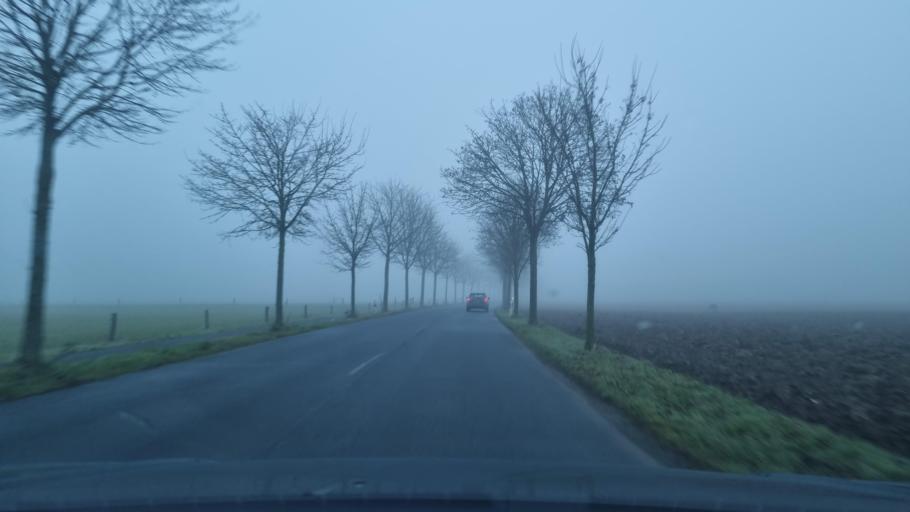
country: DE
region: North Rhine-Westphalia
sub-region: Regierungsbezirk Dusseldorf
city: Kleve
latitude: 51.7854
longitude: 6.1772
